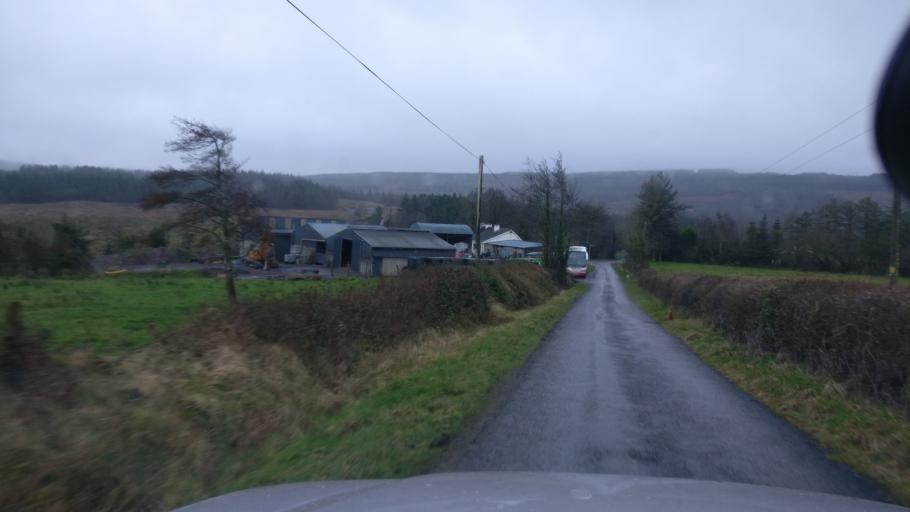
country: IE
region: Connaught
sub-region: County Galway
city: Loughrea
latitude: 53.1538
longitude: -8.6369
